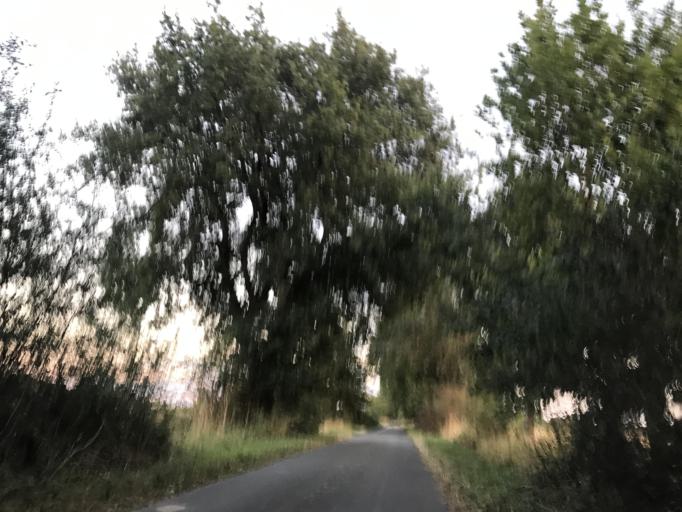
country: DE
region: Lower Saxony
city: Reinstorf
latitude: 53.2313
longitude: 10.5978
